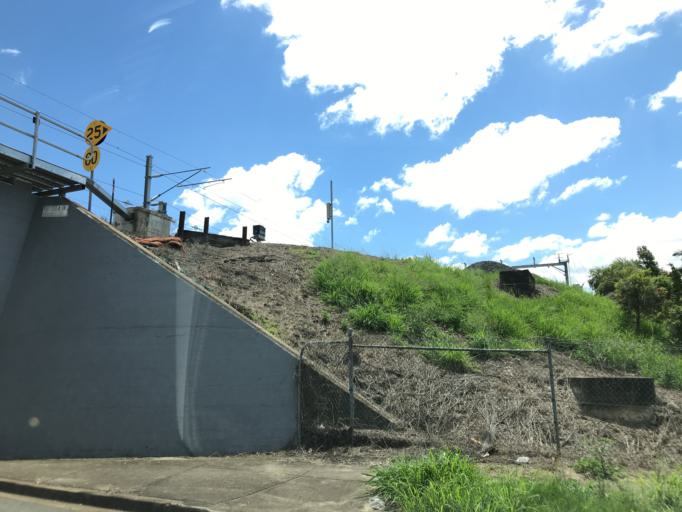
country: AU
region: Queensland
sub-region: Brisbane
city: Seventeen Mile Rocks
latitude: -27.5461
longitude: 152.9794
